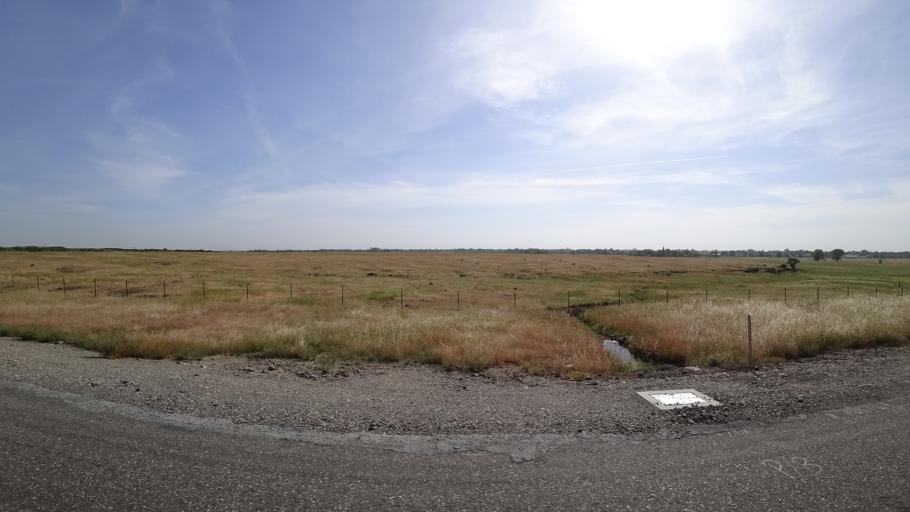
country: US
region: California
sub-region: Butte County
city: Durham
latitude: 39.6638
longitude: -121.7415
